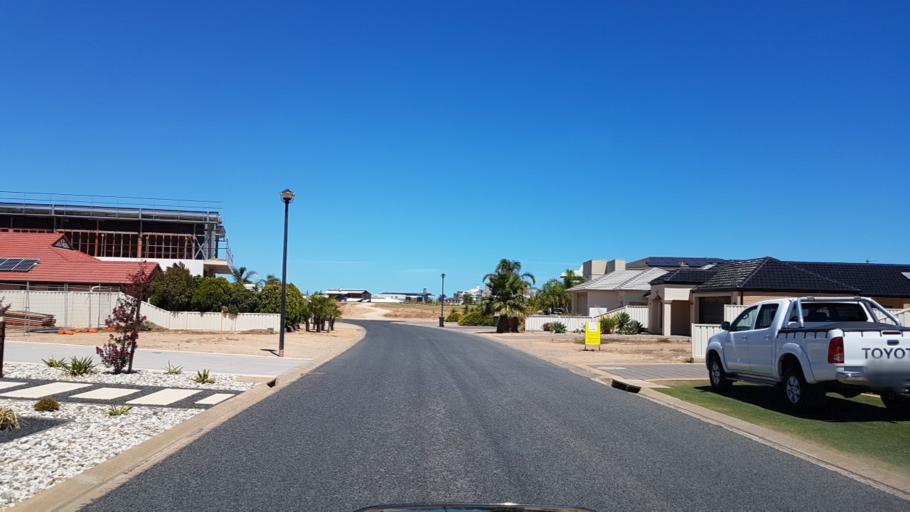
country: AU
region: South Australia
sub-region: Copper Coast
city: Wallaroo
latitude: -33.9191
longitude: 137.6391
